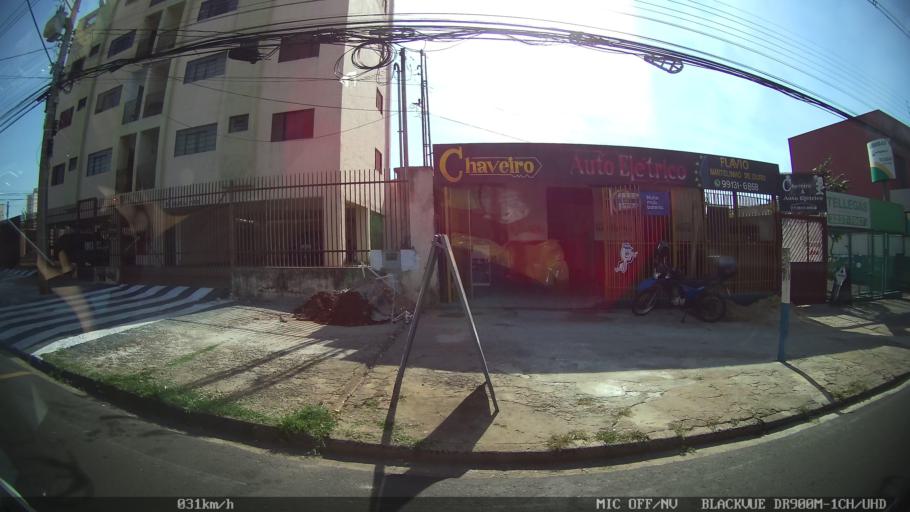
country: BR
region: Sao Paulo
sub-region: Sao Jose Do Rio Preto
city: Sao Jose do Rio Preto
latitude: -20.7949
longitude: -49.4085
